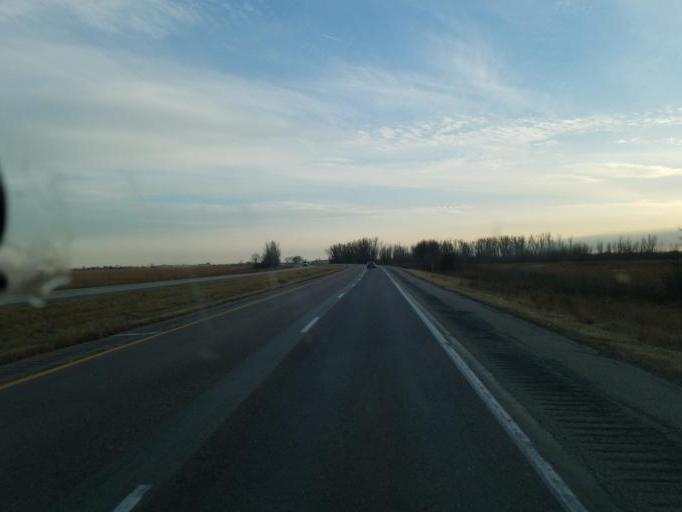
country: US
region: Nebraska
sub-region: Washington County
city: Blair
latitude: 41.6841
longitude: -96.0414
